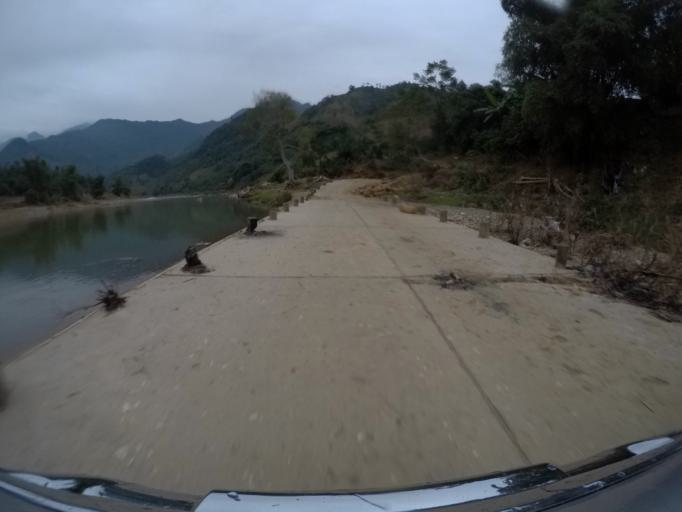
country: VN
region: Yen Bai
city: Son Thinh
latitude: 21.6817
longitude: 104.6149
